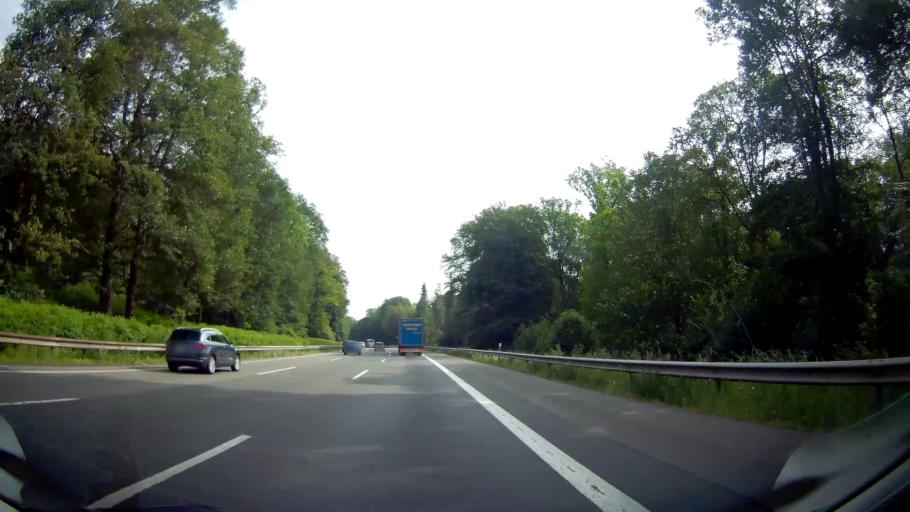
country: DE
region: North Rhine-Westphalia
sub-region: Regierungsbezirk Detmold
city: Bad Salzuflen
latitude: 52.1118
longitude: 8.7352
